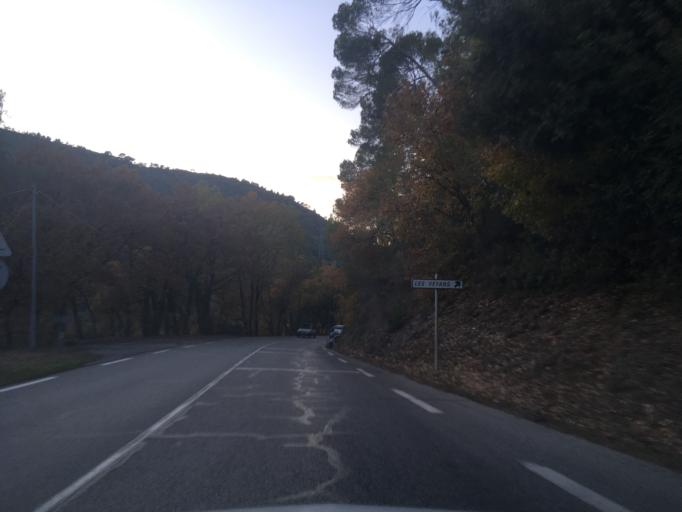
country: FR
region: Provence-Alpes-Cote d'Azur
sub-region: Departement des Alpes-Maritimes
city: Le Tignet
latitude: 43.6251
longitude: 6.8258
